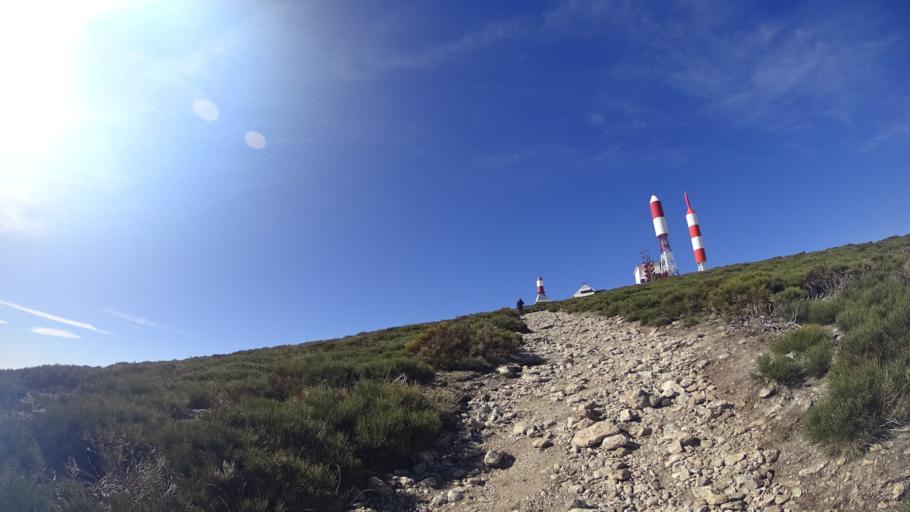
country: ES
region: Madrid
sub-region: Provincia de Madrid
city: Navacerrada
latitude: 40.7841
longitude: -3.9771
